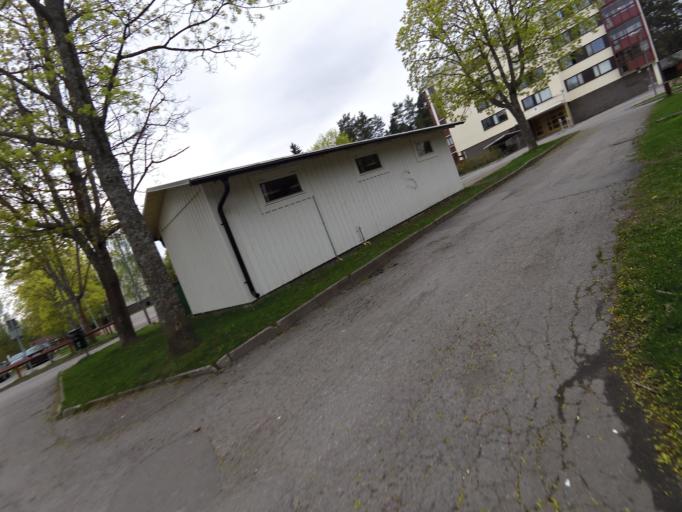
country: SE
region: Gaevleborg
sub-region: Gavle Kommun
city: Gavle
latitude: 60.6869
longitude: 17.1246
